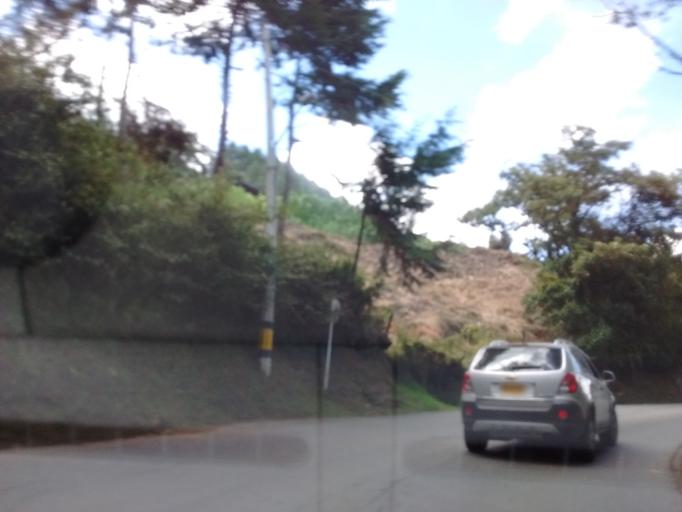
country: CO
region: Antioquia
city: Medellin
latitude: 6.2406
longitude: -75.5115
